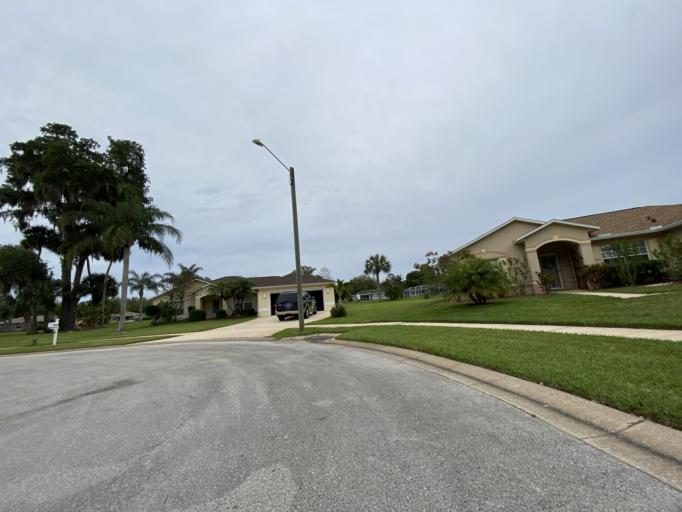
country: US
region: Florida
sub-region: Volusia County
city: South Daytona
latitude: 29.1516
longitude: -81.0021
